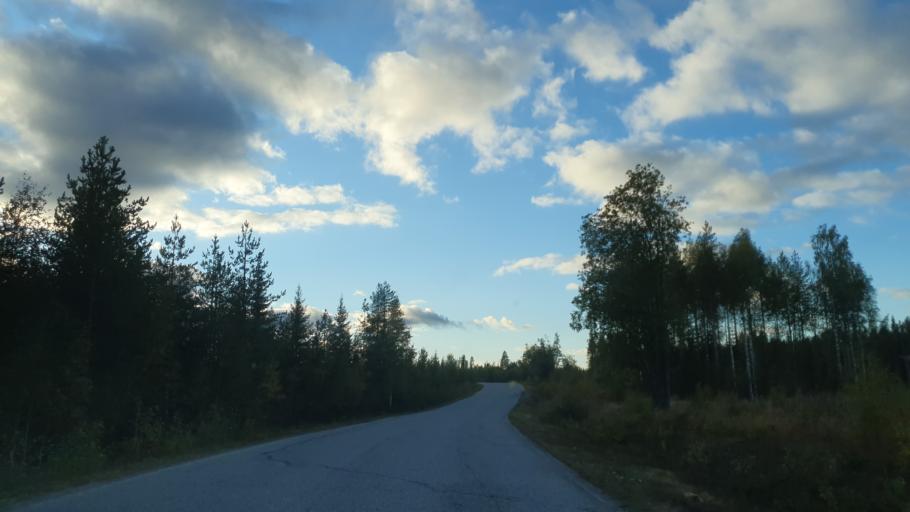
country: FI
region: Kainuu
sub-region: Kehys-Kainuu
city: Kuhmo
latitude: 63.9503
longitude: 29.7517
